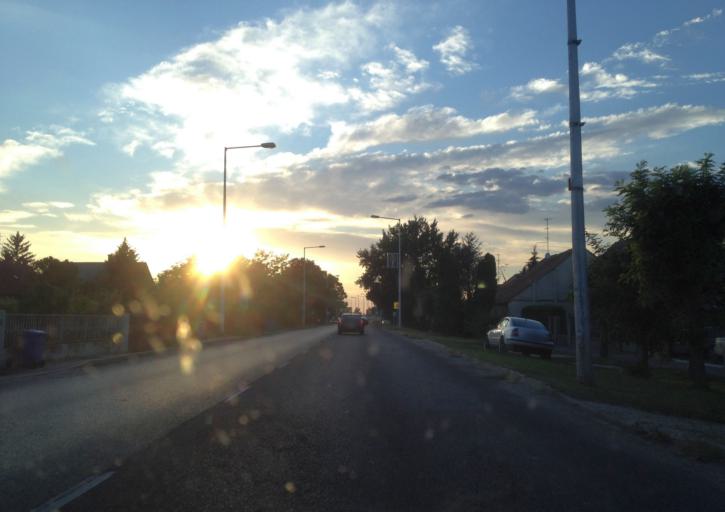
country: HU
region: Gyor-Moson-Sopron
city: Mosonmagyarovar
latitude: 47.8743
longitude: 17.2655
